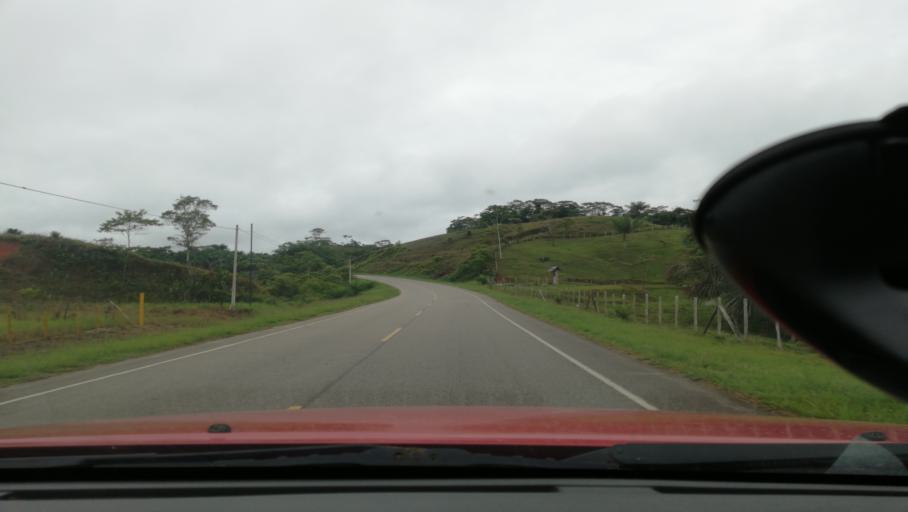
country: PE
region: Loreto
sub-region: Provincia de Loreto
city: Nauta
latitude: -4.4964
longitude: -73.5946
